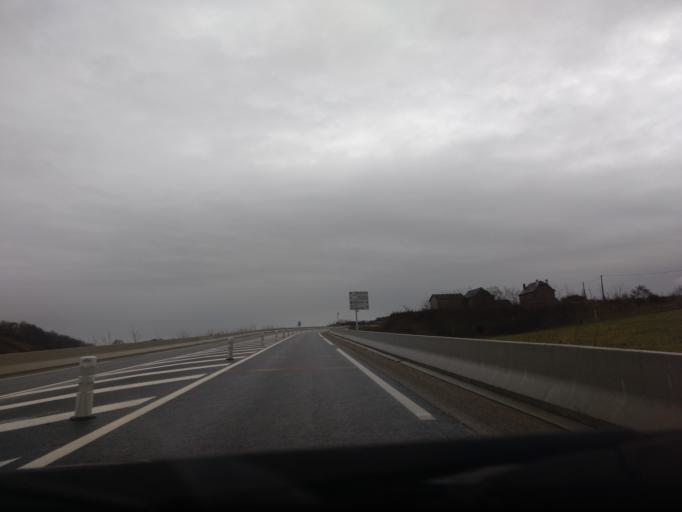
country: FR
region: Midi-Pyrenees
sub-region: Departement de l'Aveyron
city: Firmi
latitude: 44.5152
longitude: 2.3546
